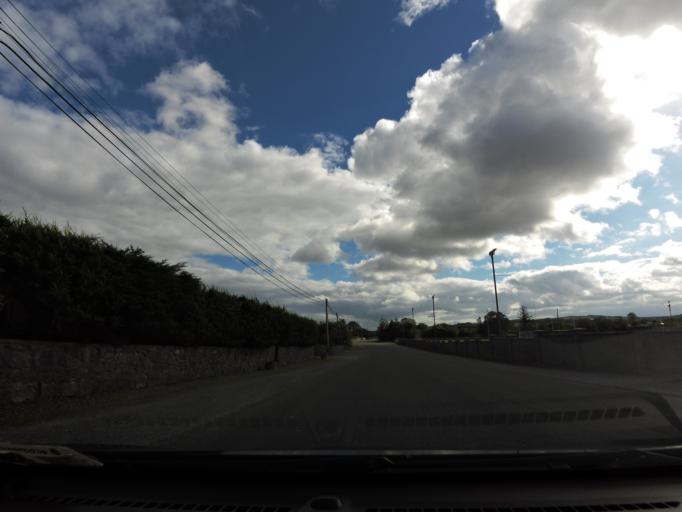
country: IE
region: Connaught
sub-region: County Galway
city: Moycullen
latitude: 53.3594
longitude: -9.1744
